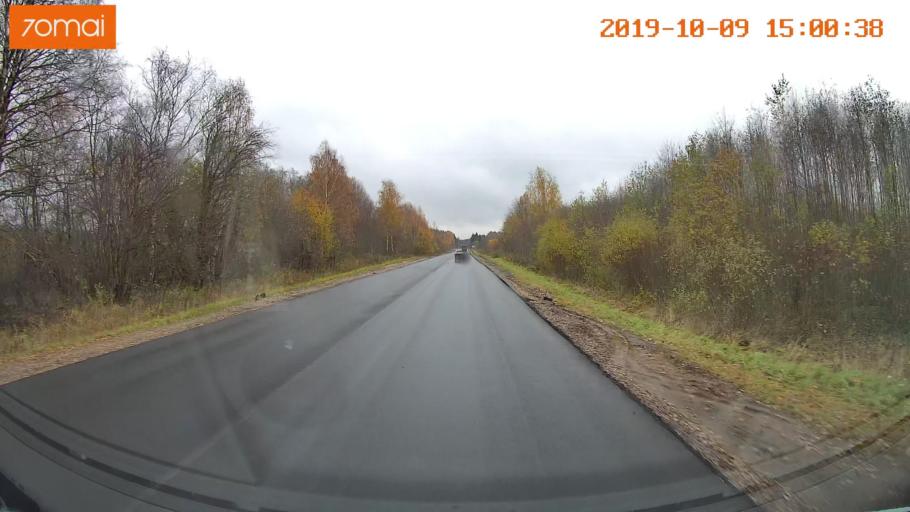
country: RU
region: Kostroma
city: Chistyye Bory
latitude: 58.3070
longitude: 41.6785
